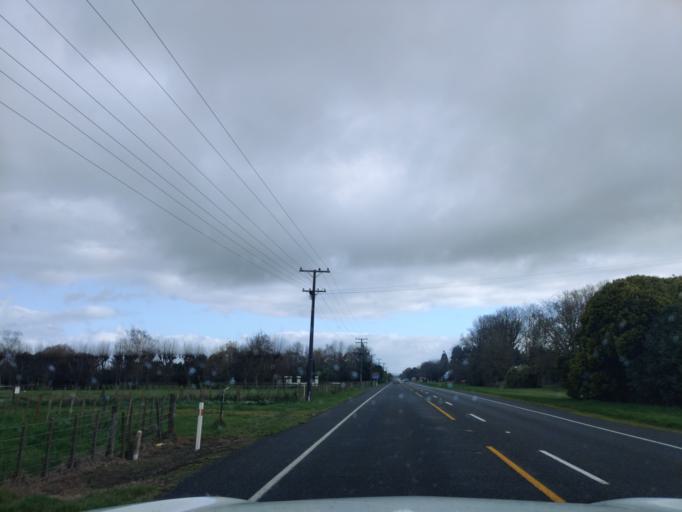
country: NZ
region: Manawatu-Wanganui
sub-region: Palmerston North City
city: Palmerston North
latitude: -40.3289
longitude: 175.5859
